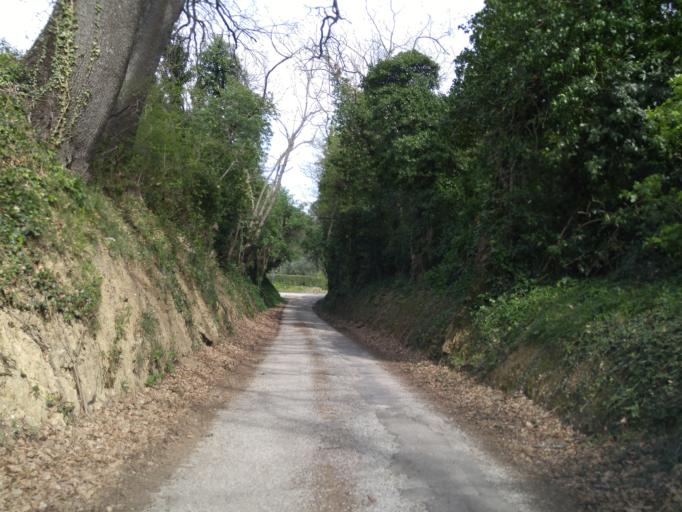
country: IT
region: The Marches
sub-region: Provincia di Pesaro e Urbino
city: Cartoceto
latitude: 43.7638
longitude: 12.8919
